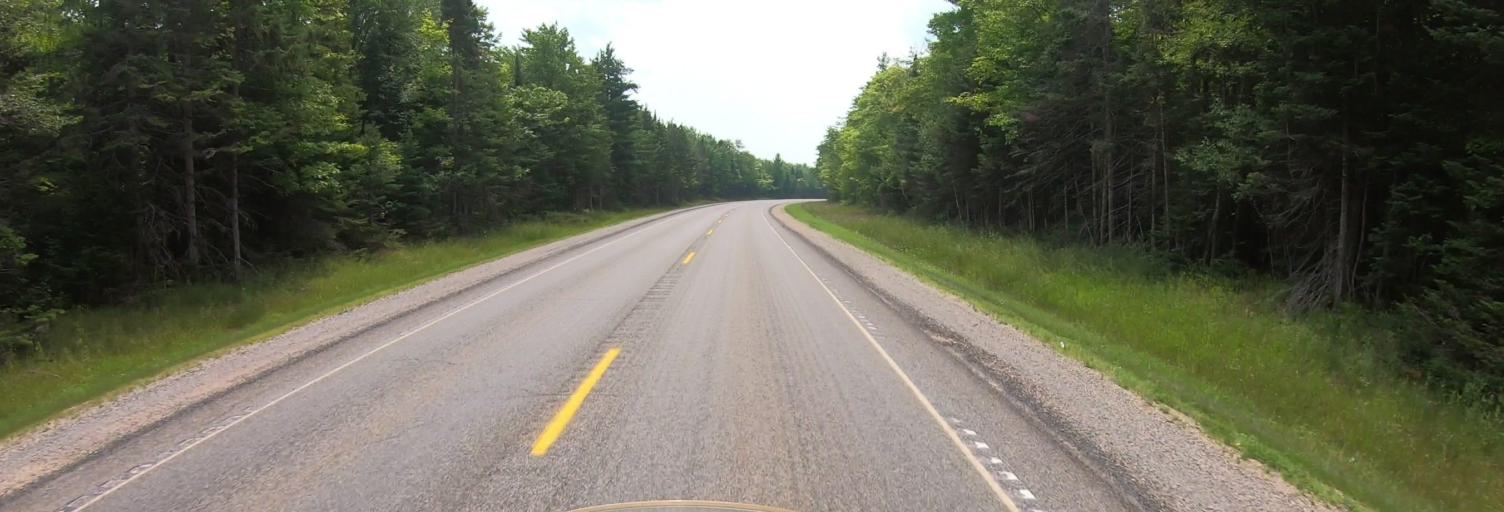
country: US
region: Michigan
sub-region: Alger County
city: Munising
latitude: 46.3393
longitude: -86.7334
